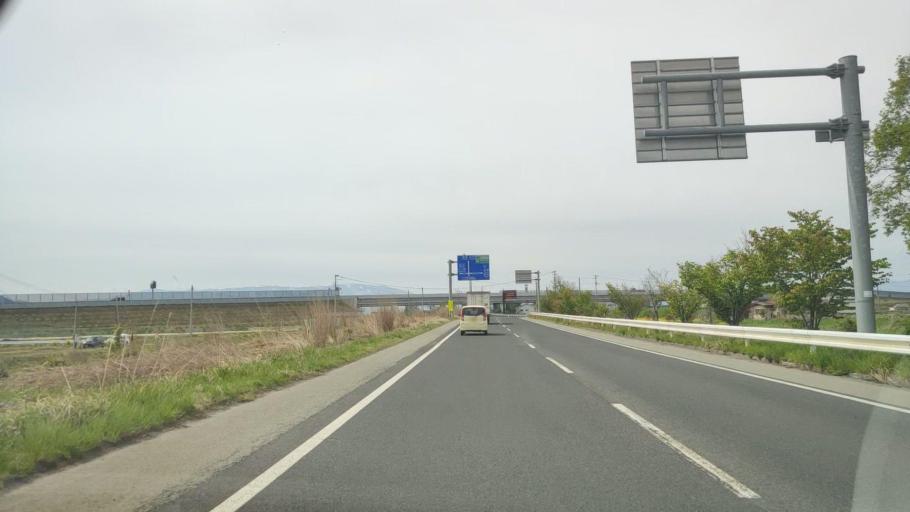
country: JP
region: Yamagata
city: Takahata
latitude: 38.0301
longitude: 140.1708
